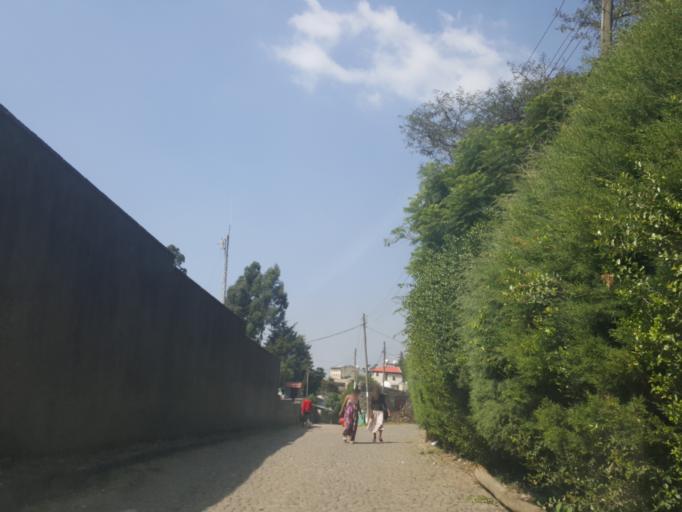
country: ET
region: Adis Abeba
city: Addis Ababa
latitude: 9.0530
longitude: 38.7340
